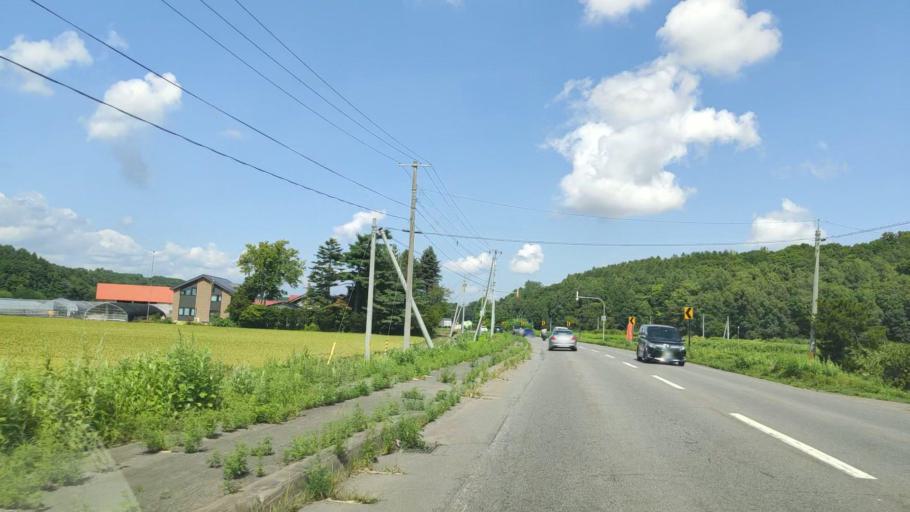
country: JP
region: Hokkaido
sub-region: Asahikawa-shi
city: Asahikawa
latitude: 43.6276
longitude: 142.4649
